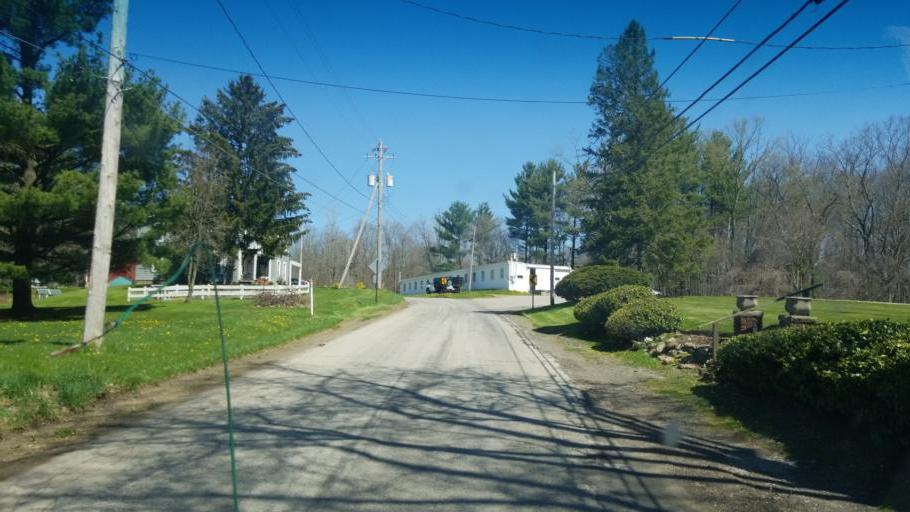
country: US
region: Ohio
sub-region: Richland County
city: Lincoln Heights
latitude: 40.8230
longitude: -82.4361
